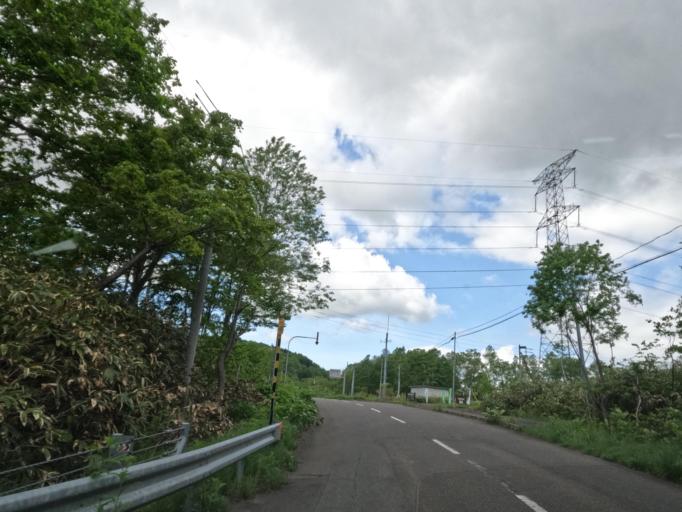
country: JP
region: Hokkaido
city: Tobetsu
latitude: 43.4658
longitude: 141.5994
